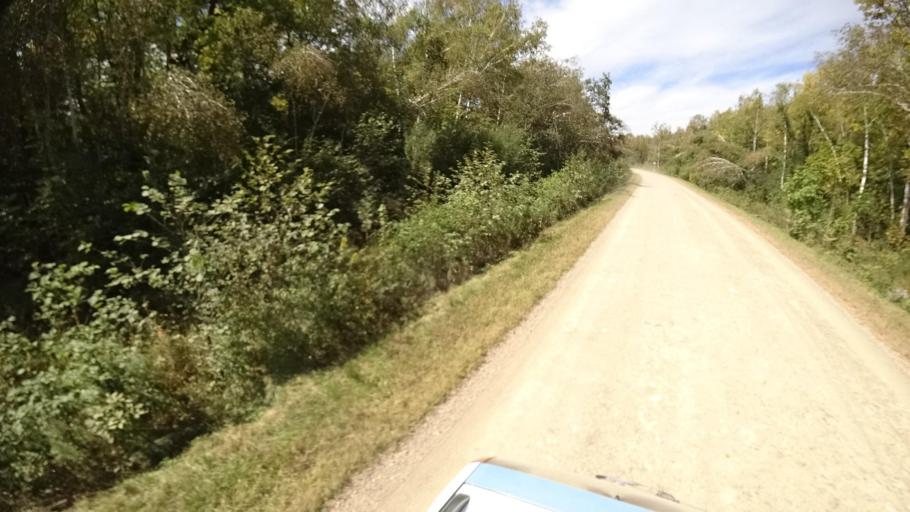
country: RU
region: Primorskiy
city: Yakovlevka
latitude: 44.6627
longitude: 133.7245
